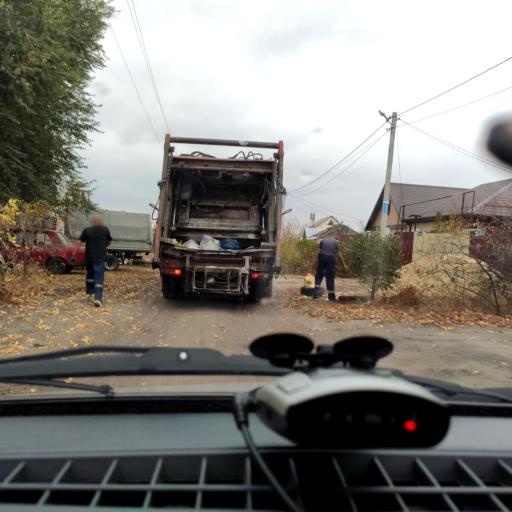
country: RU
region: Voronezj
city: Pridonskoy
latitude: 51.7018
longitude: 39.0716
